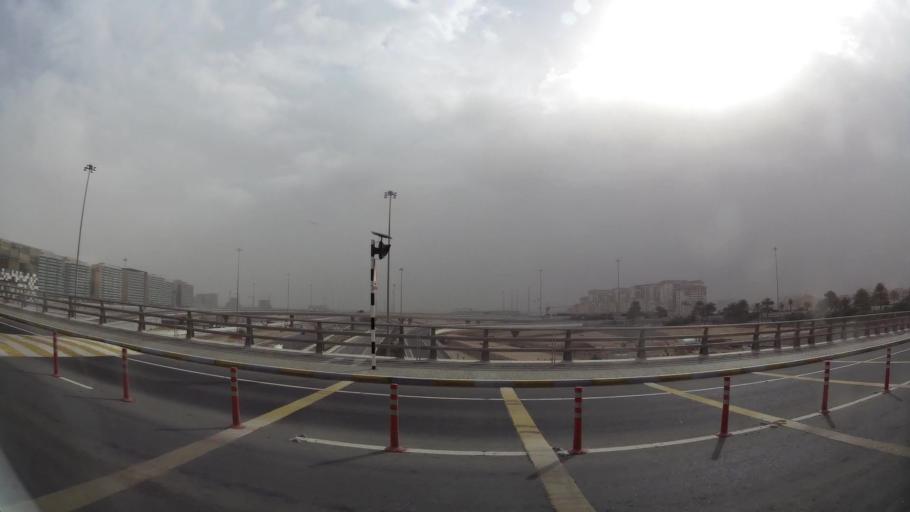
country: AE
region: Abu Dhabi
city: Abu Dhabi
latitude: 24.4446
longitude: 54.6008
